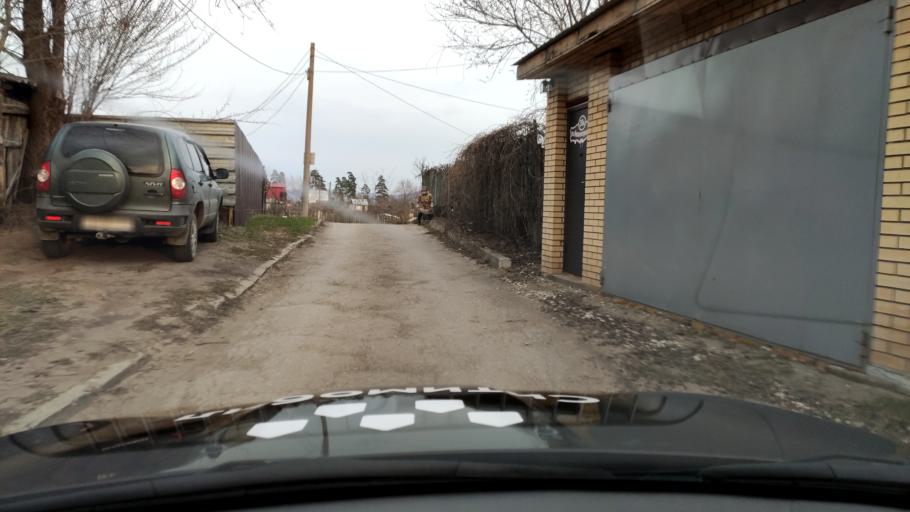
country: RU
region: Samara
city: Zhigulevsk
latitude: 53.4760
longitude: 49.5389
